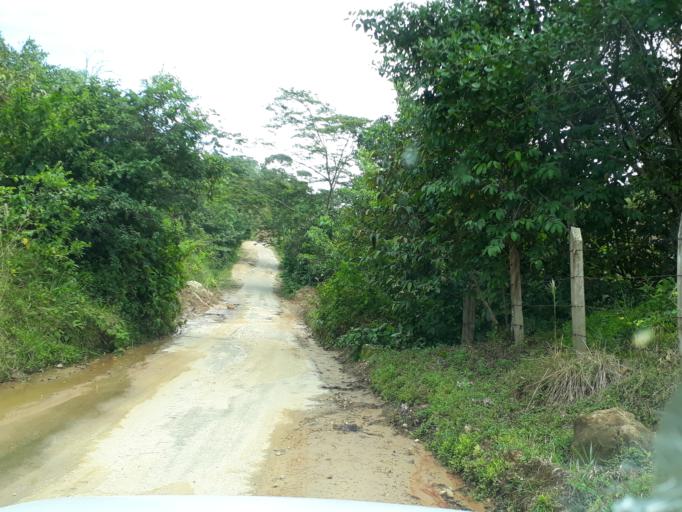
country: CO
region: Cundinamarca
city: Medina
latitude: 4.5958
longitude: -73.3033
